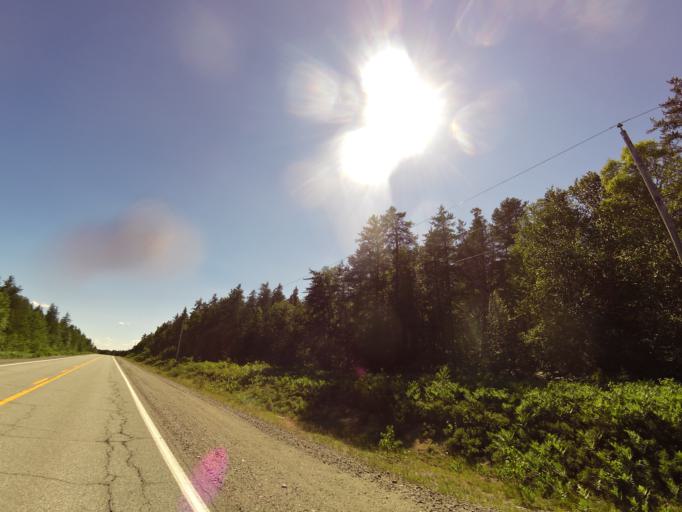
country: CA
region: Quebec
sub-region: Abitibi-Temiscamingue
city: Senneterre
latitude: 48.1416
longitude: -77.3714
